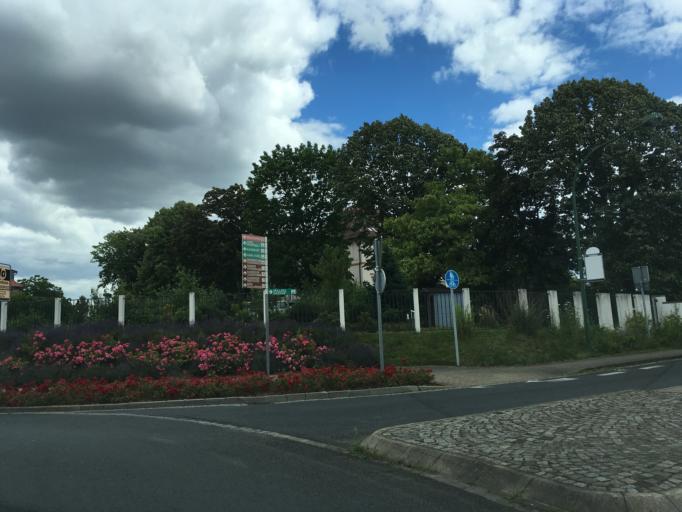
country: DE
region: Saxony
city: Radeberg
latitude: 51.1056
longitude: 13.9220
